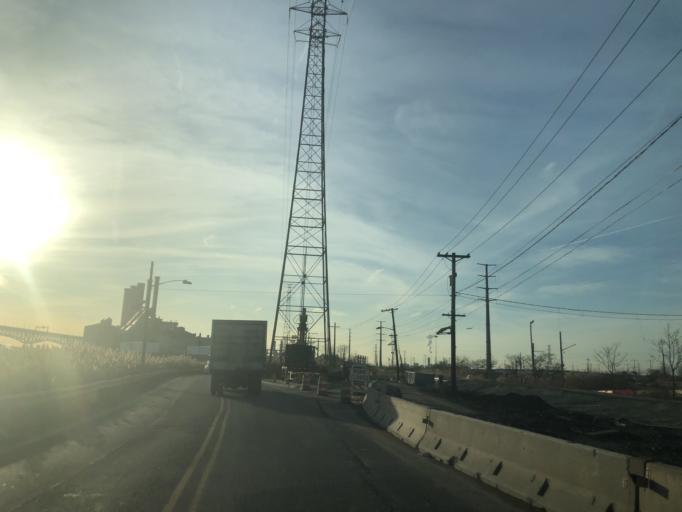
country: US
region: New Jersey
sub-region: Hudson County
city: Jersey City
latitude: 40.7404
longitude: -74.0896
